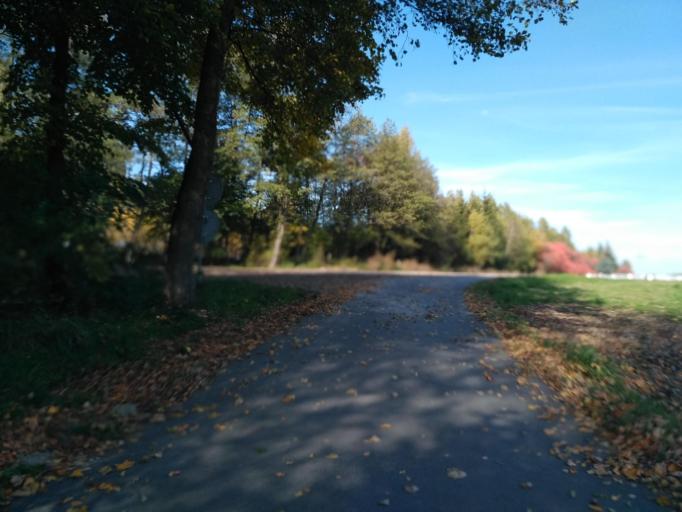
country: PL
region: Subcarpathian Voivodeship
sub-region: Powiat rzeszowski
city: Trzciana
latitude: 50.0760
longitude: 21.7930
